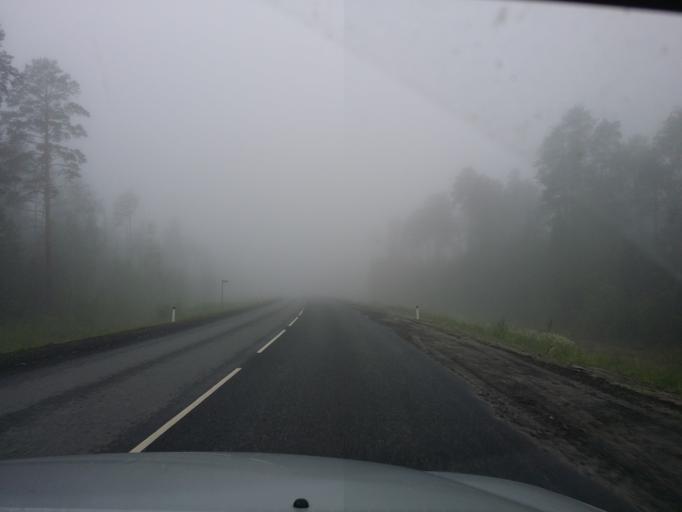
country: RU
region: Khanty-Mansiyskiy Avtonomnyy Okrug
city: Gornopravdinsk
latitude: 59.6923
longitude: 70.0835
